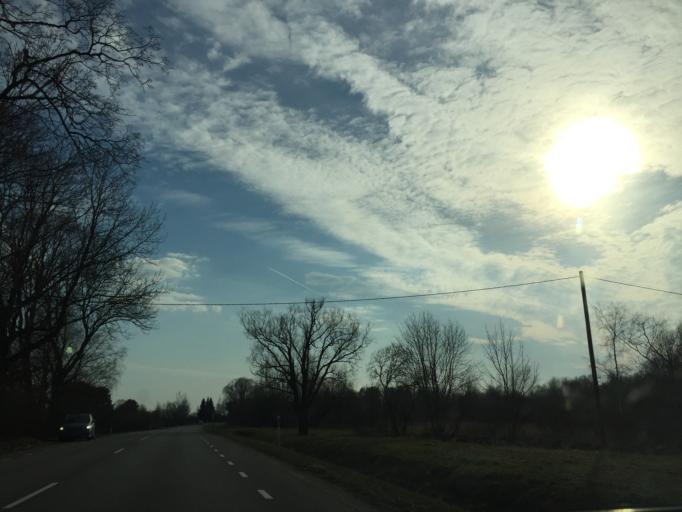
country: EE
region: Jogevamaa
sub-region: Mustvee linn
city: Mustvee
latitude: 58.9070
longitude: 26.9994
